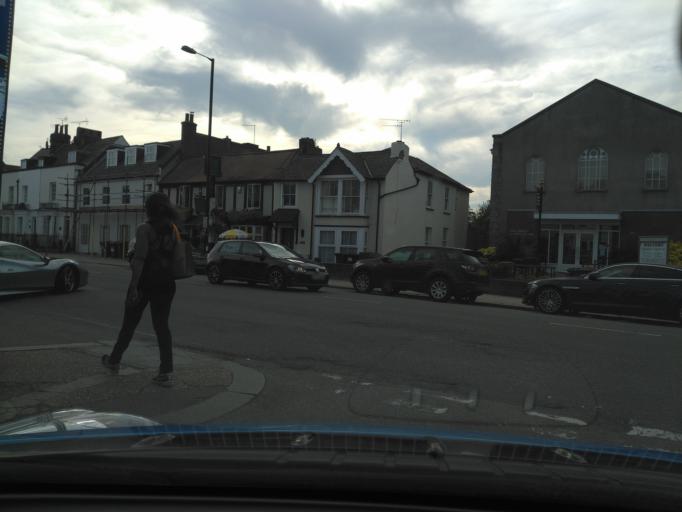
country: GB
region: England
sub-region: Greater London
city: High Barnet
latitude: 51.6583
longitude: -0.2008
